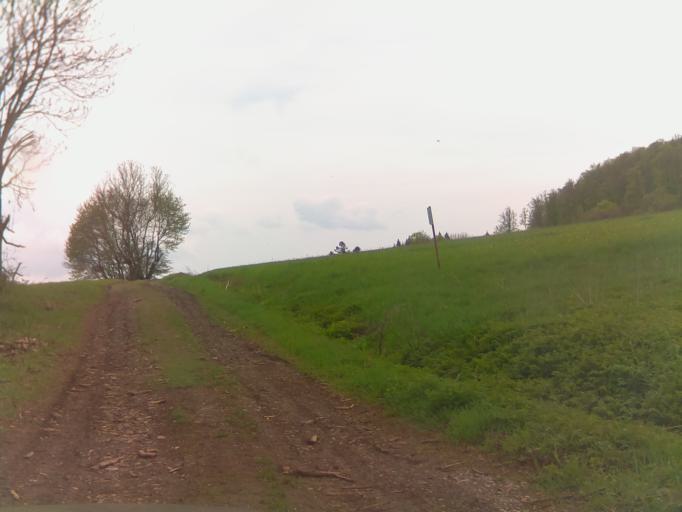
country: DE
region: Thuringia
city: Oepfershausen
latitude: 50.6298
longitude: 10.2370
